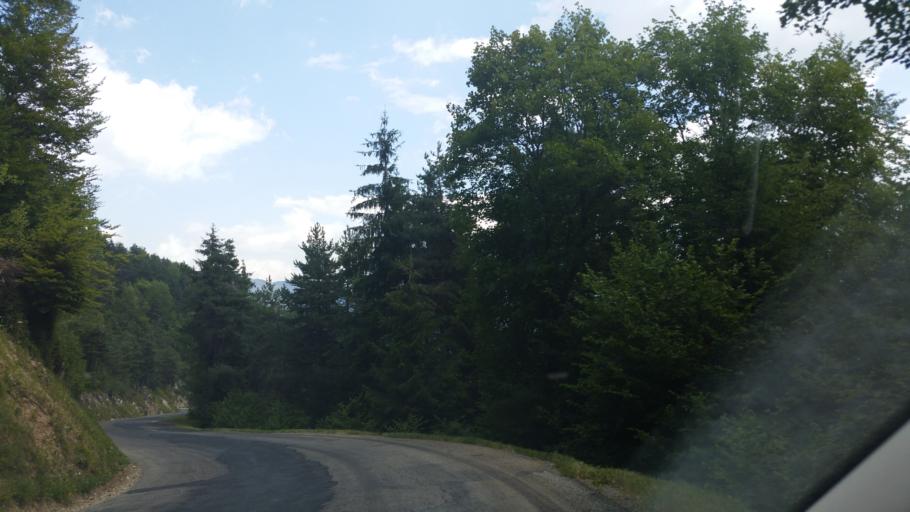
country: FR
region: Rhone-Alpes
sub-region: Departement de la Savoie
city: Saint-Jean-de-Maurienne
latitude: 45.2315
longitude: 6.3045
